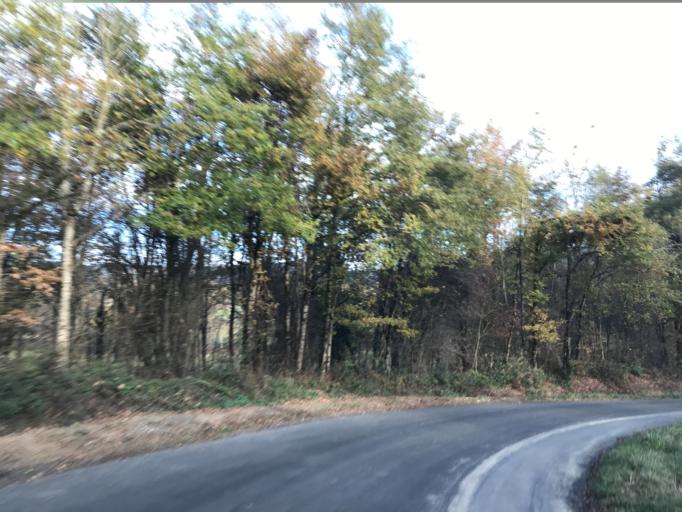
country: FR
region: Auvergne
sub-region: Departement du Puy-de-Dome
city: Courpiere
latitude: 45.7567
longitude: 3.5931
